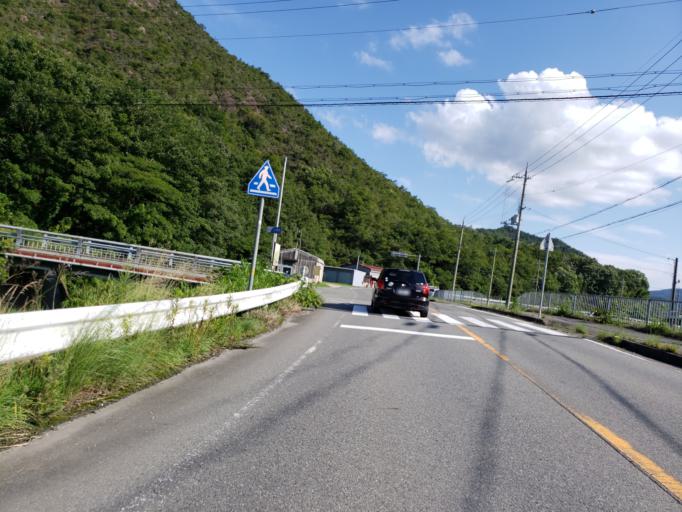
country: JP
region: Hyogo
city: Kakogawacho-honmachi
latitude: 34.8804
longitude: 134.7996
